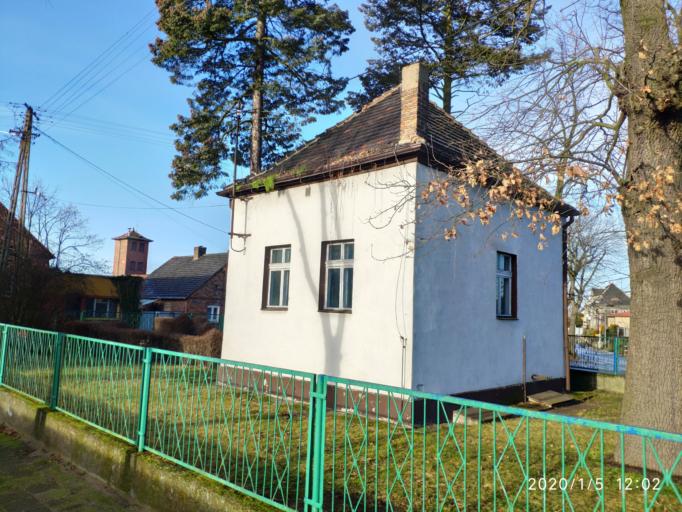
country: PL
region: Lubusz
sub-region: Powiat zielonogorski
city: Czerwiensk
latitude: 52.0136
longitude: 15.4191
